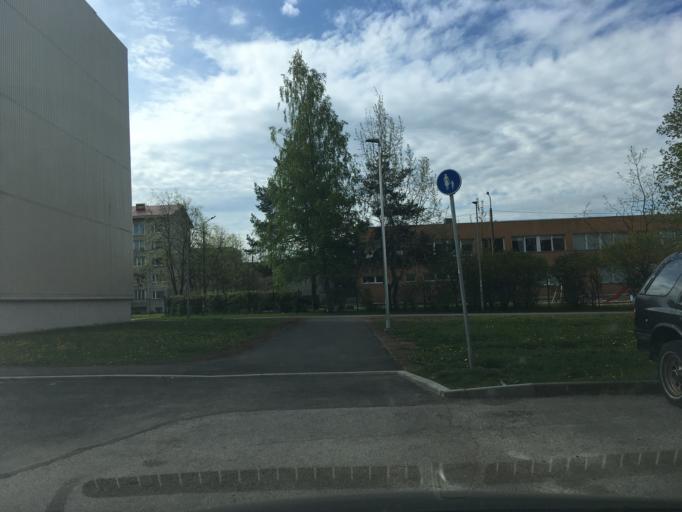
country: EE
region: Harju
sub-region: Tallinna linn
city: Kose
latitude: 59.4385
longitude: 24.8333
